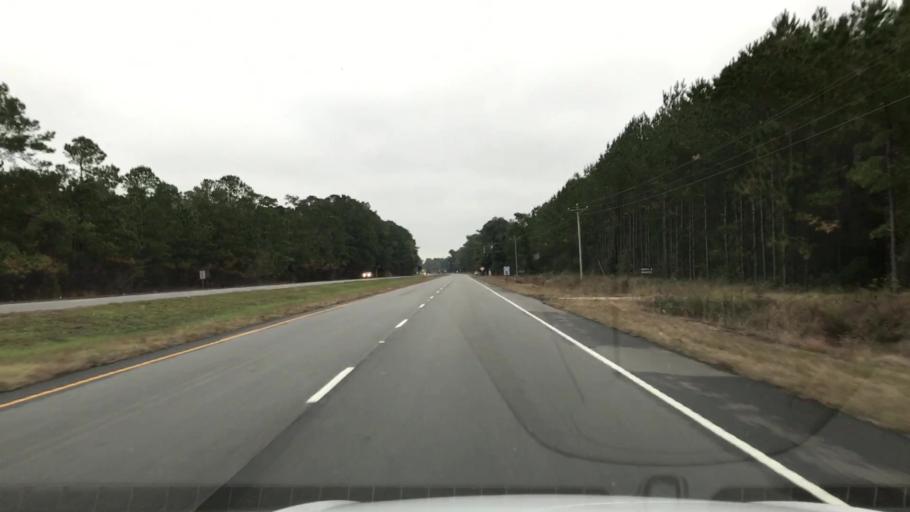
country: US
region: South Carolina
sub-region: Charleston County
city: Awendaw
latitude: 33.0864
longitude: -79.4907
